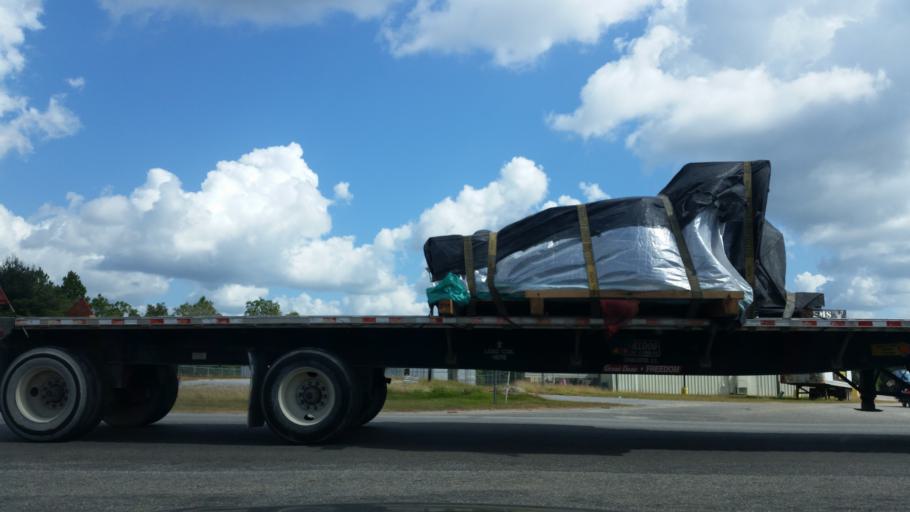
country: US
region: Alabama
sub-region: Baldwin County
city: Robertsdale
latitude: 30.6305
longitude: -87.6155
